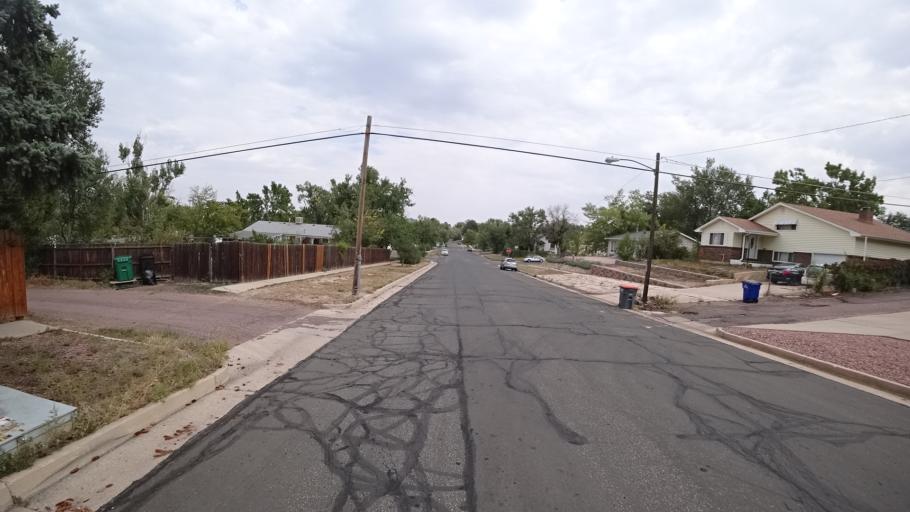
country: US
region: Colorado
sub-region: El Paso County
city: Colorado Springs
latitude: 38.8503
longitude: -104.7867
